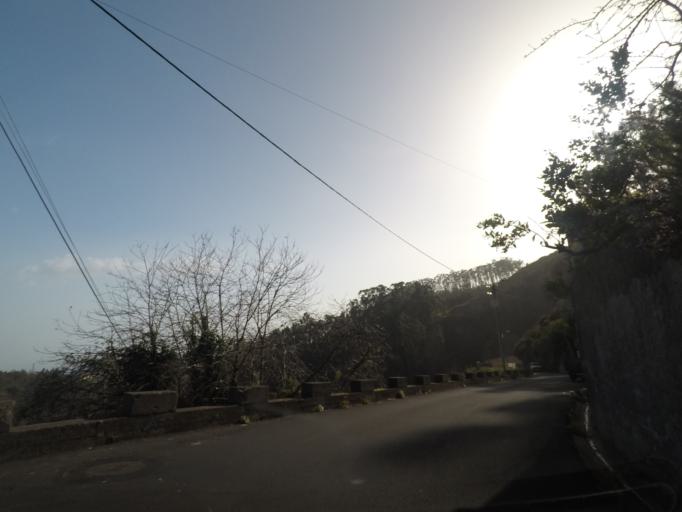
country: PT
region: Madeira
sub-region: Ribeira Brava
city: Campanario
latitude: 32.6755
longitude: -17.0057
